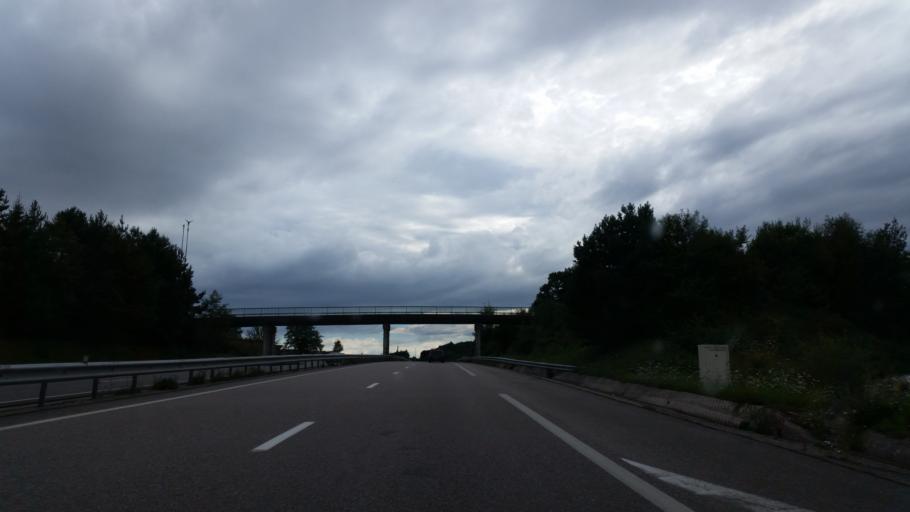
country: FR
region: Lorraine
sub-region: Departement des Vosges
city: Remiremont
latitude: 48.0039
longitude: 6.5553
